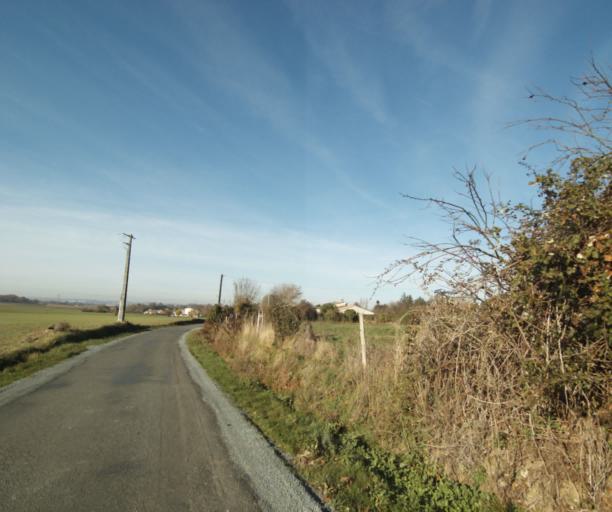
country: FR
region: Poitou-Charentes
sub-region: Departement de la Charente-Maritime
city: Chaniers
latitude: 45.7399
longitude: -0.5713
